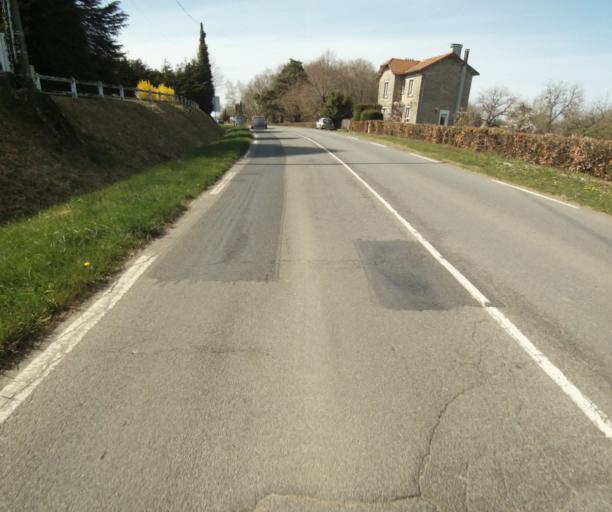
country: FR
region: Limousin
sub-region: Departement de la Correze
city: Seilhac
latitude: 45.3573
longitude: 1.7307
